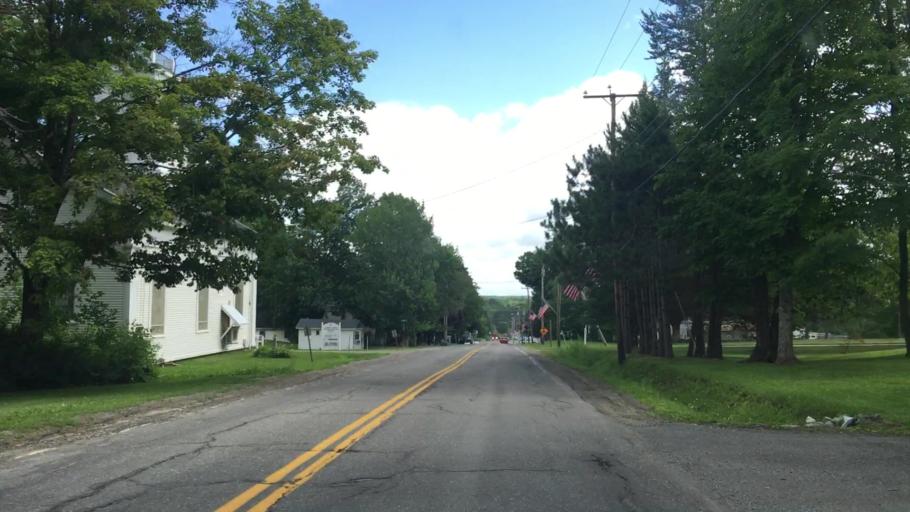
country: US
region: Maine
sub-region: Penobscot County
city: Carmel
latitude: 44.7964
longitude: -69.0550
